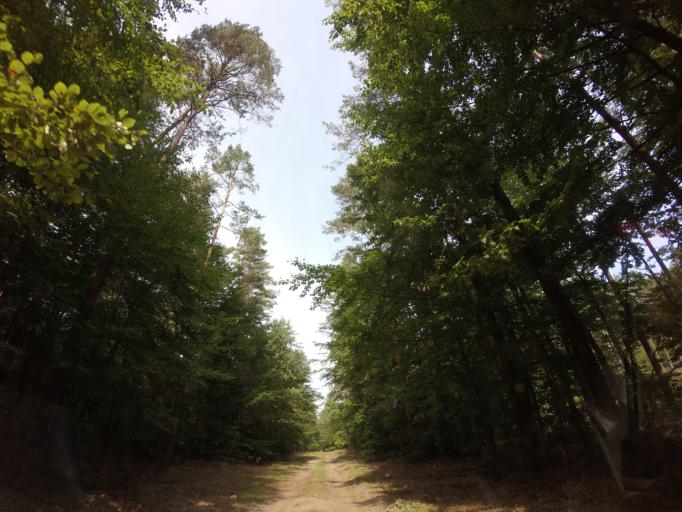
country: PL
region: West Pomeranian Voivodeship
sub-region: Powiat drawski
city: Drawsko Pomorskie
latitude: 53.4579
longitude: 15.7198
